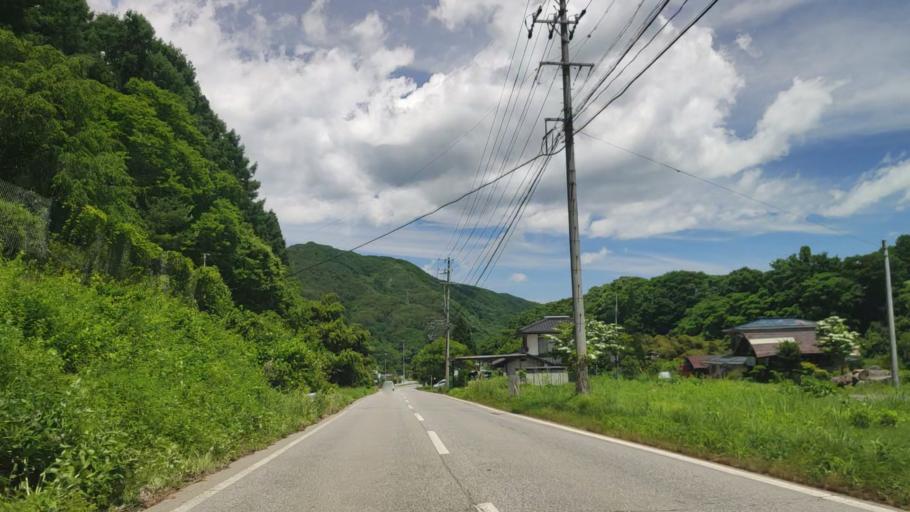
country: JP
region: Nagano
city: Kamimaruko
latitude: 36.1962
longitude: 138.2430
